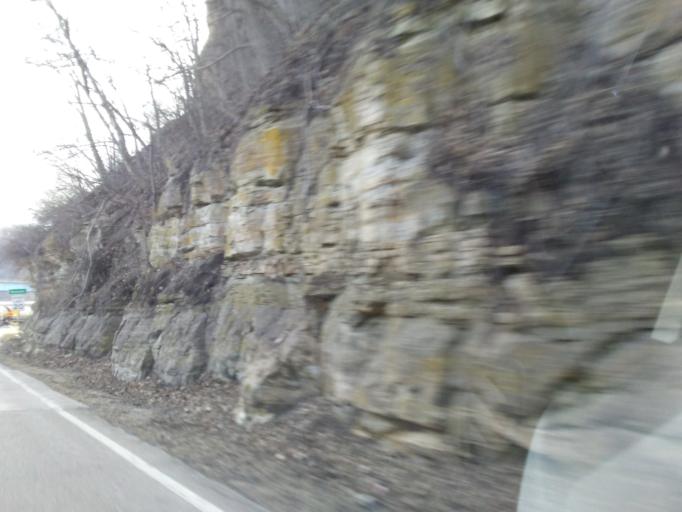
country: US
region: Wisconsin
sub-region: Crawford County
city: Prairie du Chien
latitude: 43.0462
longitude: -91.1773
